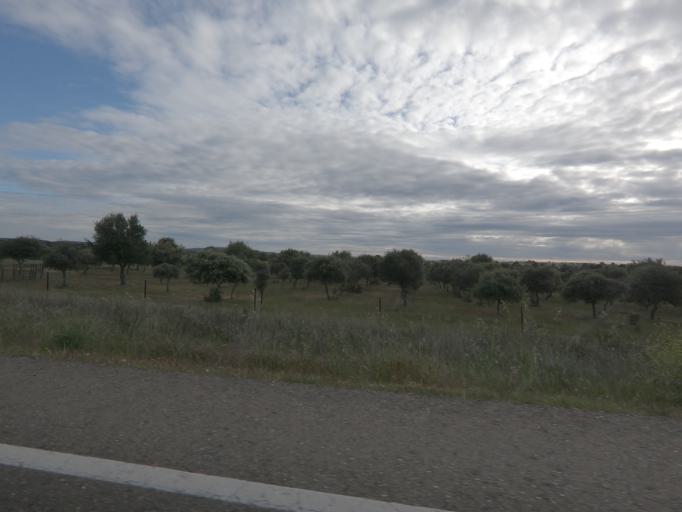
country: ES
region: Extremadura
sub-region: Provincia de Caceres
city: Torrejoncillo
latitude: 39.9275
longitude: -6.5016
